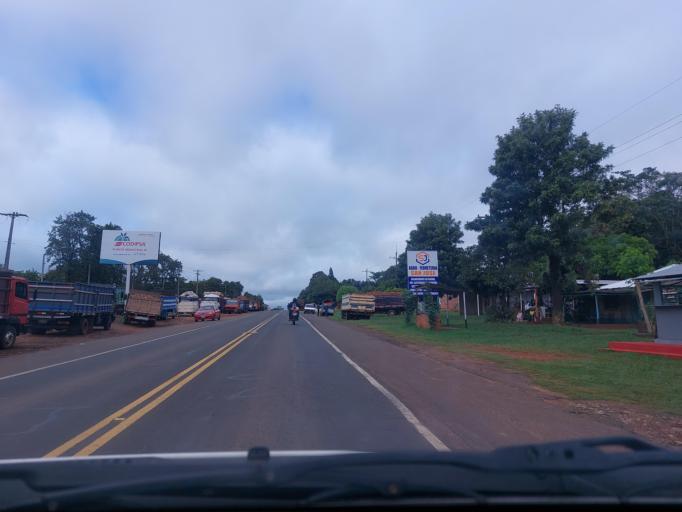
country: PY
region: San Pedro
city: Guayaybi
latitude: -24.5699
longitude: -56.4028
